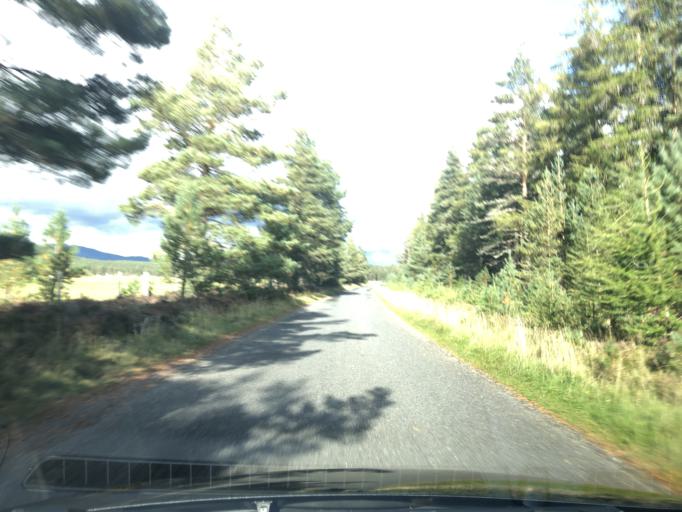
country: GB
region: Scotland
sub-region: Highland
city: Aviemore
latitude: 57.1041
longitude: -3.8888
